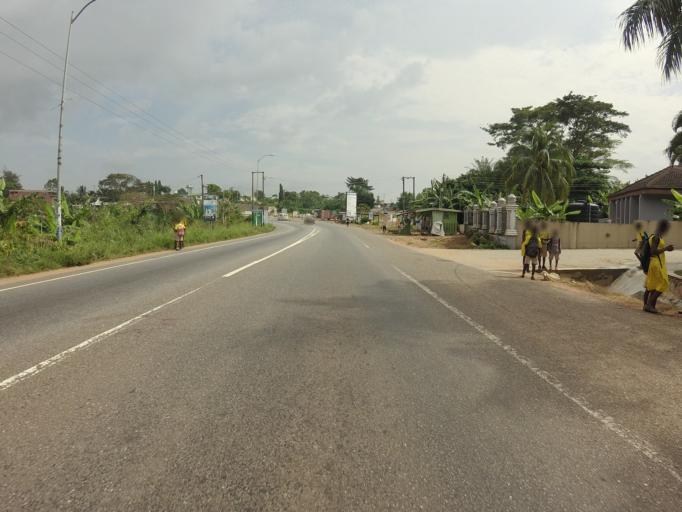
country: GH
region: Eastern
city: Aburi
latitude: 5.8083
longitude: -0.1839
